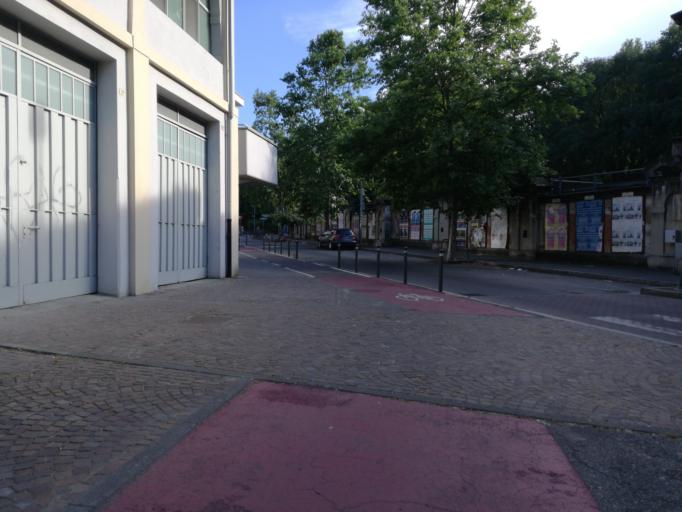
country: IT
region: Piedmont
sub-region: Provincia di Novara
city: Novara
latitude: 45.4487
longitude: 8.6140
